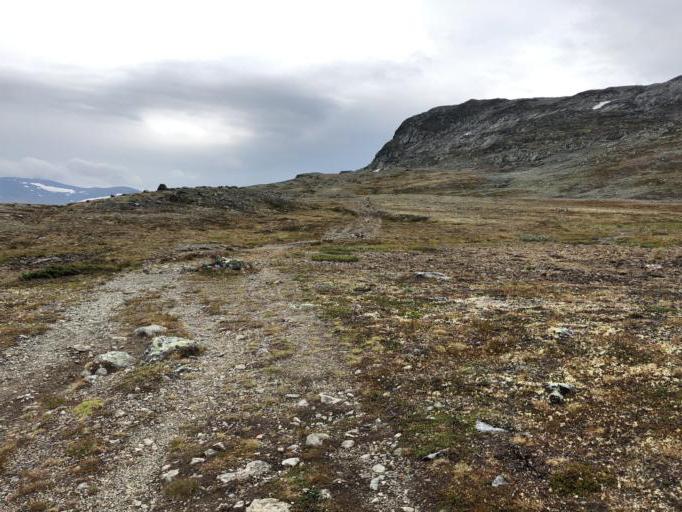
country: NO
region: Oppland
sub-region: Lom
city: Fossbergom
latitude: 61.5206
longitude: 8.8108
